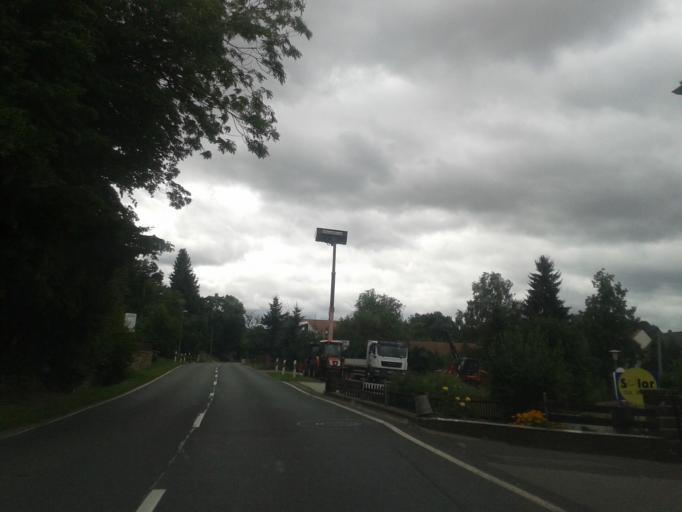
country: DE
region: Saxony
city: Wilsdruff
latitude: 51.0230
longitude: 13.5559
